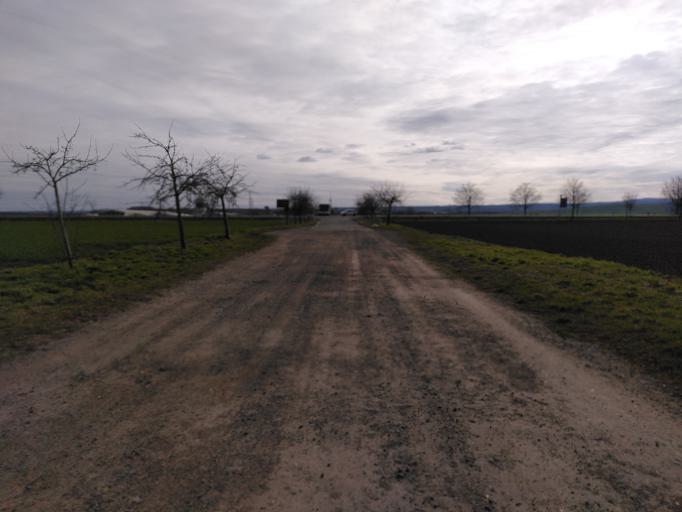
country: DE
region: Saxony-Anhalt
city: Gatersleben
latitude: 51.7873
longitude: 11.2538
